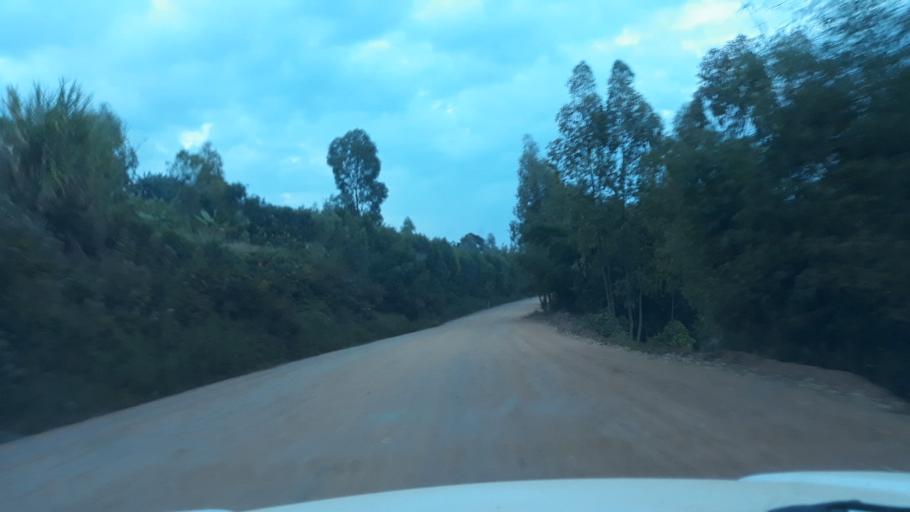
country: CD
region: South Kivu
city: Bukavu
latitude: -2.5724
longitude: 28.8549
